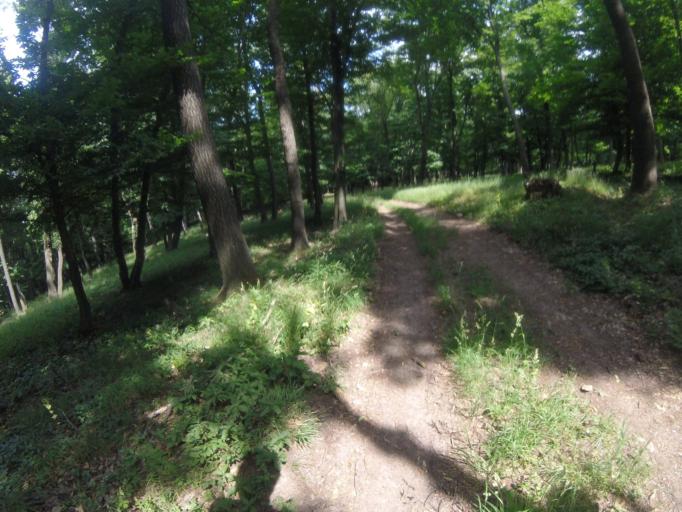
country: HU
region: Fejer
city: Szarliget
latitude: 47.4886
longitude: 18.4624
